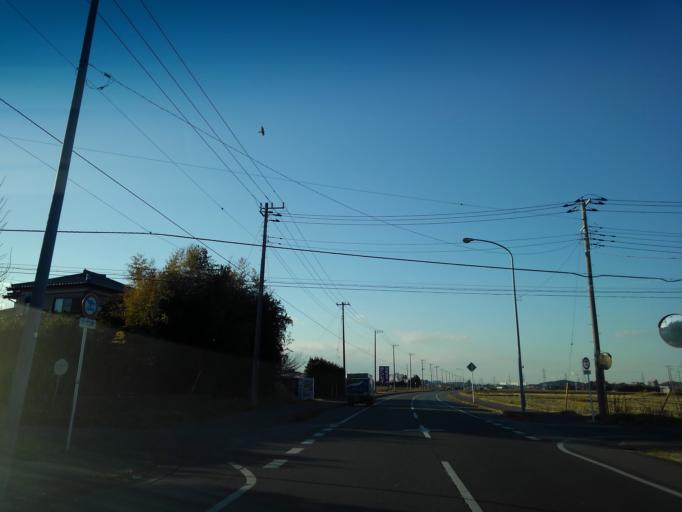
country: JP
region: Chiba
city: Kimitsu
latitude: 35.3129
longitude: 139.9159
